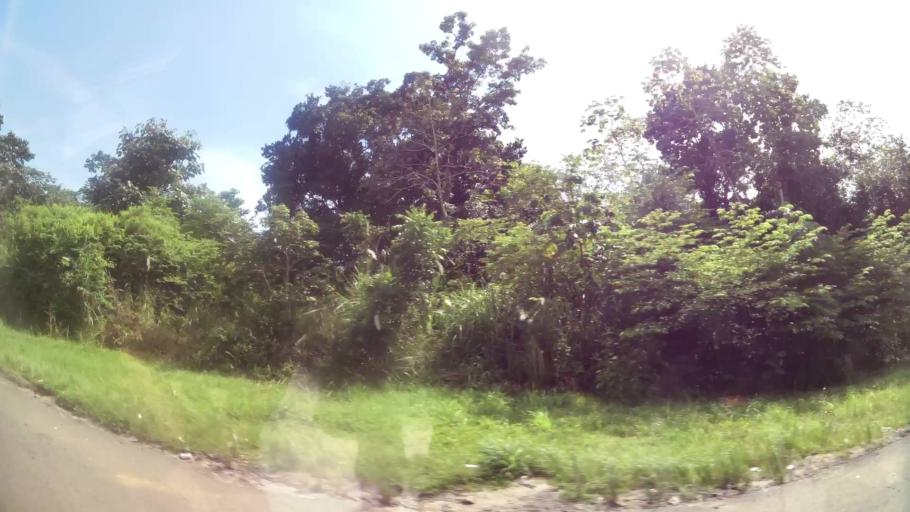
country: PA
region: Panama
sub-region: Distrito de Panama
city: Paraiso
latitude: 9.0271
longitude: -79.6085
